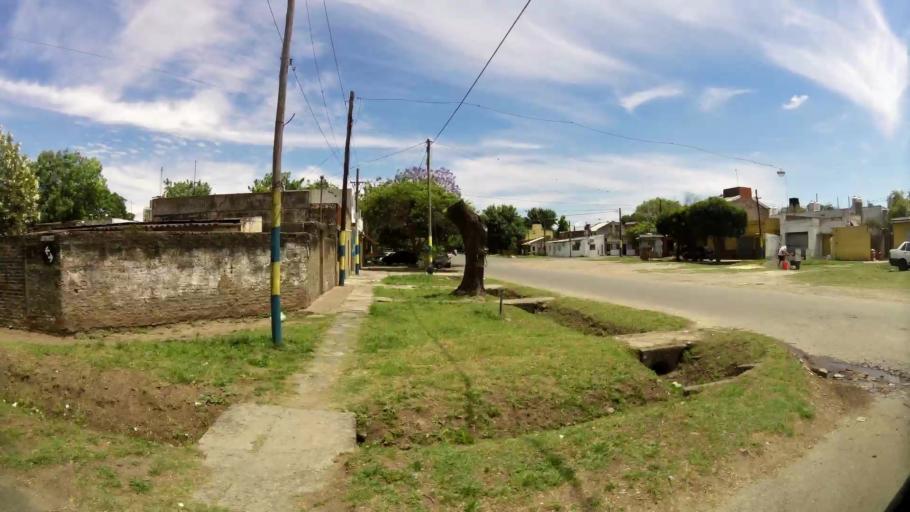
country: AR
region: Santa Fe
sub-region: Departamento de Rosario
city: Rosario
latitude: -32.9818
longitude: -60.6318
